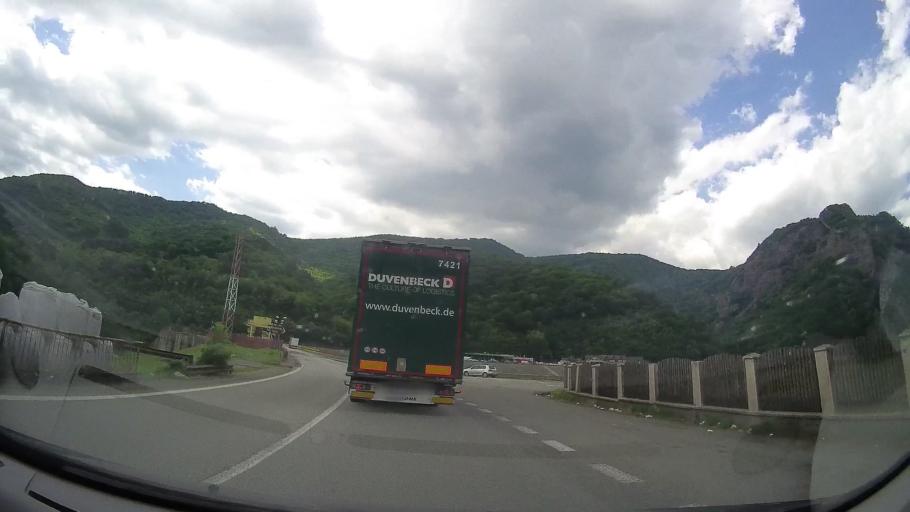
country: RO
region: Valcea
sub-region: Oras Calimanesti
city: Calimanesti
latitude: 45.2782
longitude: 24.3114
